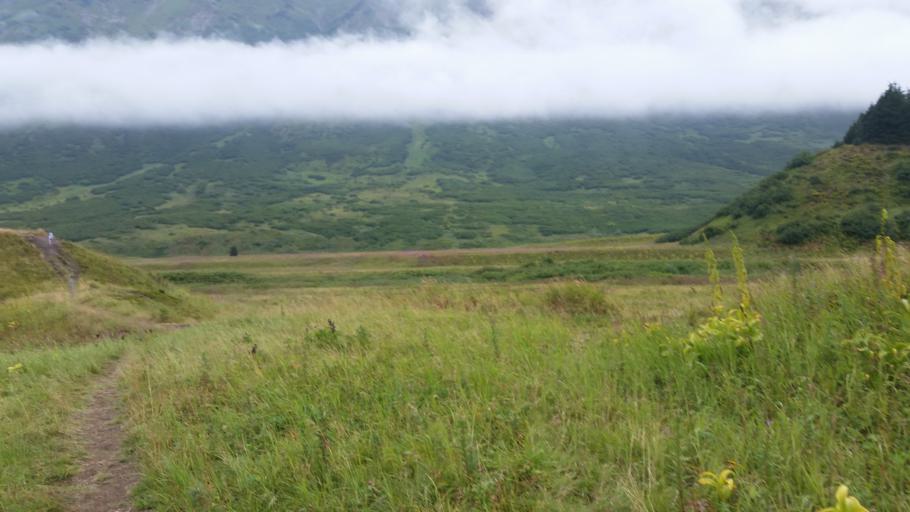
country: US
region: Alaska
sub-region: Anchorage Municipality
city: Girdwood
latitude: 60.7873
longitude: -149.2156
